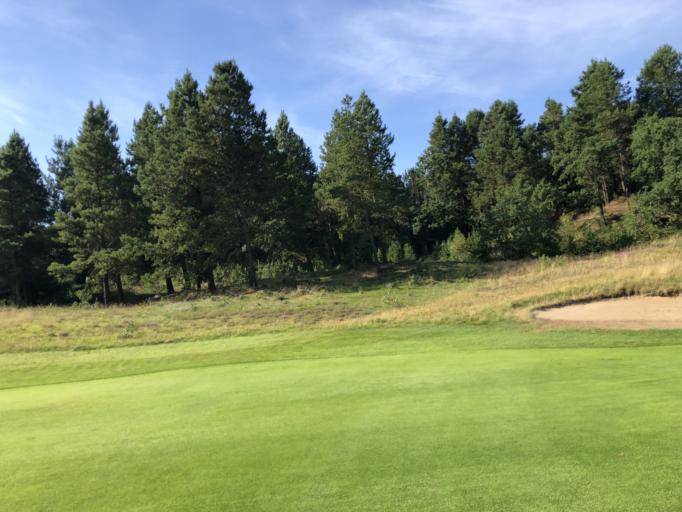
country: DK
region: Central Jutland
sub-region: Holstebro Kommune
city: Ulfborg
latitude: 56.3289
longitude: 8.4110
